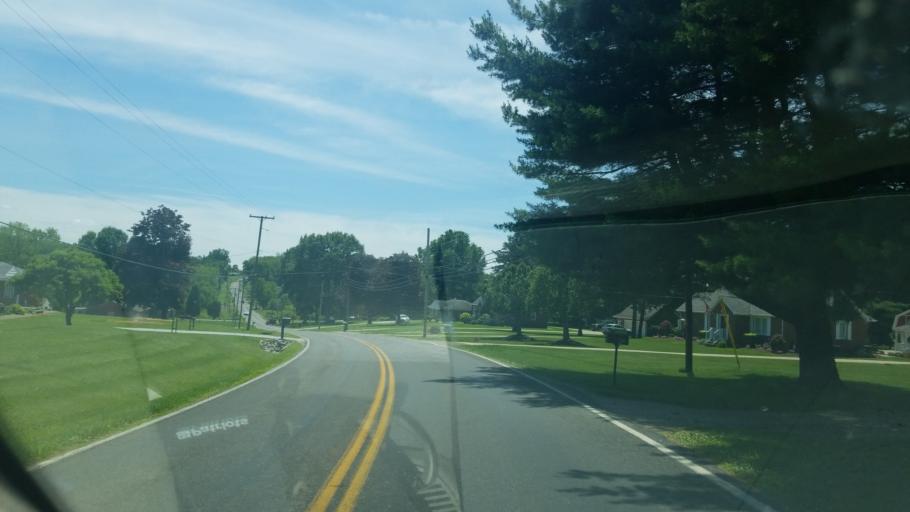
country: US
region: Ohio
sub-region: Stark County
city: Louisville
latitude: 40.8494
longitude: -81.2338
